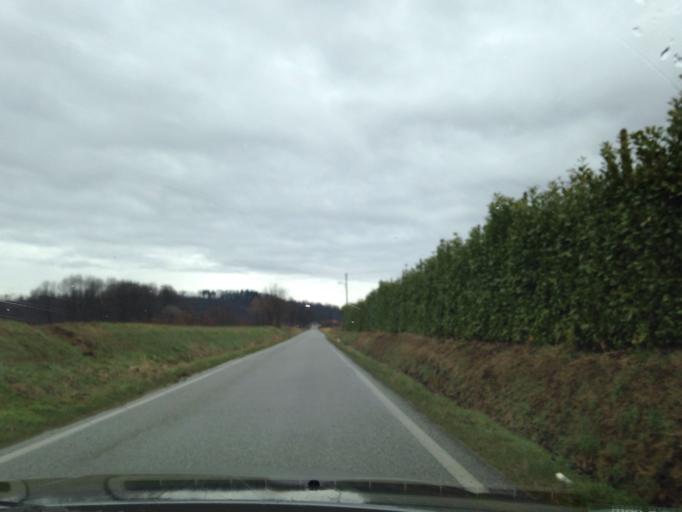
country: IT
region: Piedmont
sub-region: Provincia di Torino
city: Villareggia
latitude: 45.3125
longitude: 7.9951
